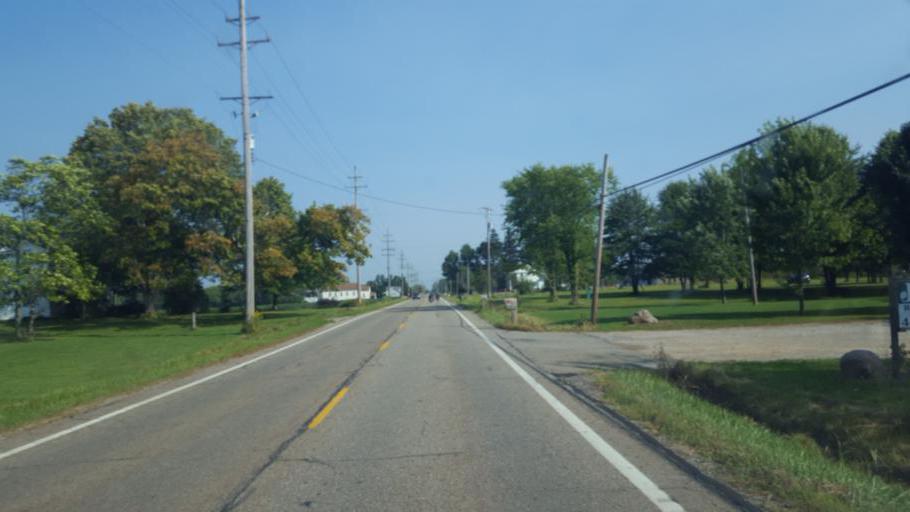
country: US
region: Ohio
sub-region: Ashtabula County
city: Orwell
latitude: 41.5884
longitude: -80.8650
